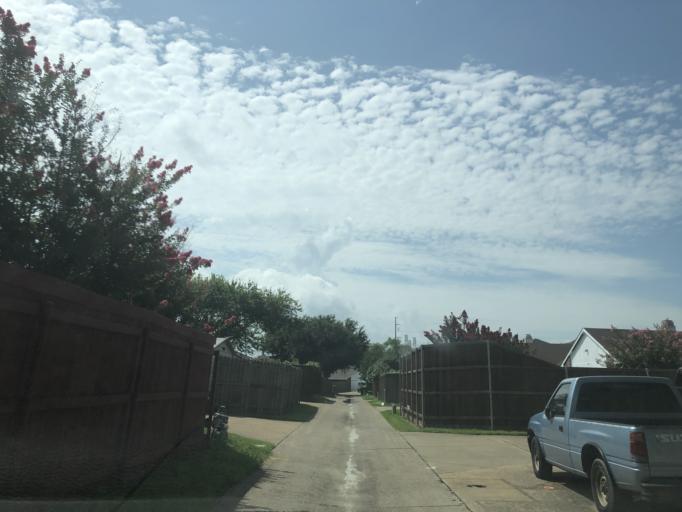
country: US
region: Texas
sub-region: Dallas County
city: Sunnyvale
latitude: 32.8369
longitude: -96.5640
